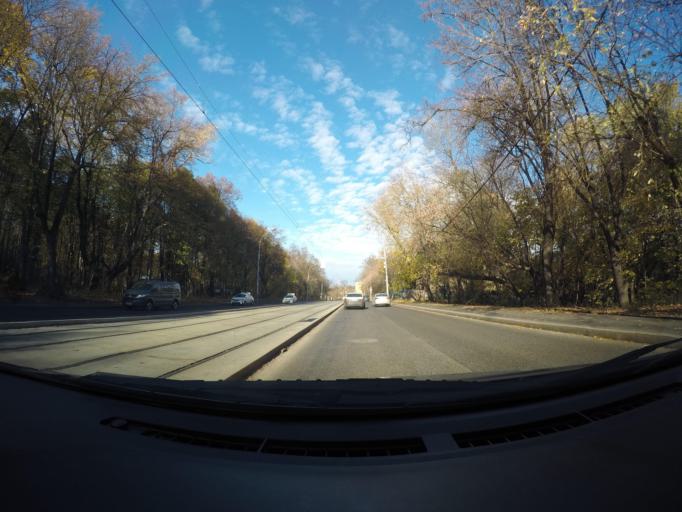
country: RU
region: Moscow
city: Sokol'niki
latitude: 55.8161
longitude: 37.6823
